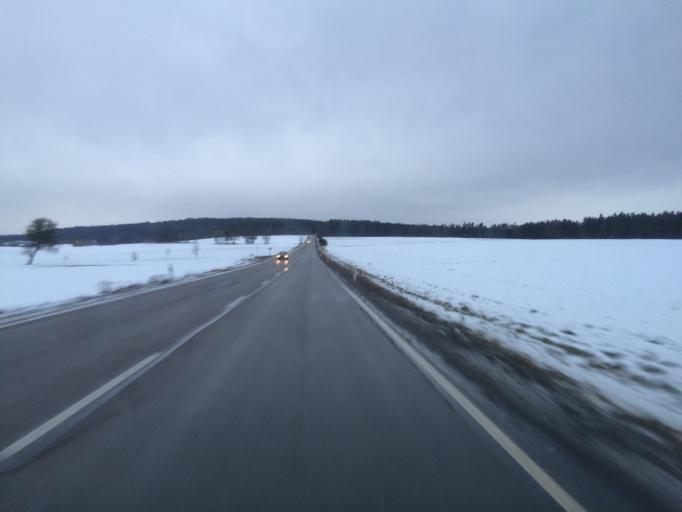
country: DE
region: Bavaria
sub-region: Upper Palatinate
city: Breitenbrunn
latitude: 49.3551
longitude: 12.0604
